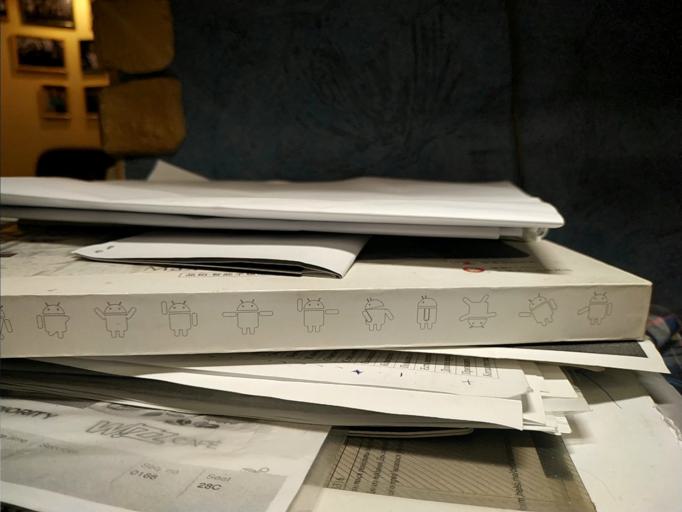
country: RU
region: Tverskaya
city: Zubtsov
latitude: 56.0787
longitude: 34.8110
